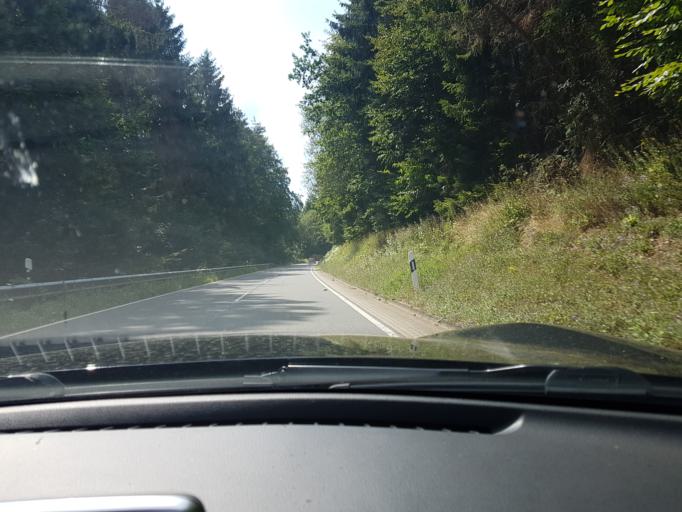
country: DE
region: Baden-Wuerttemberg
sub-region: Karlsruhe Region
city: Limbach
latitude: 49.4235
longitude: 9.2265
